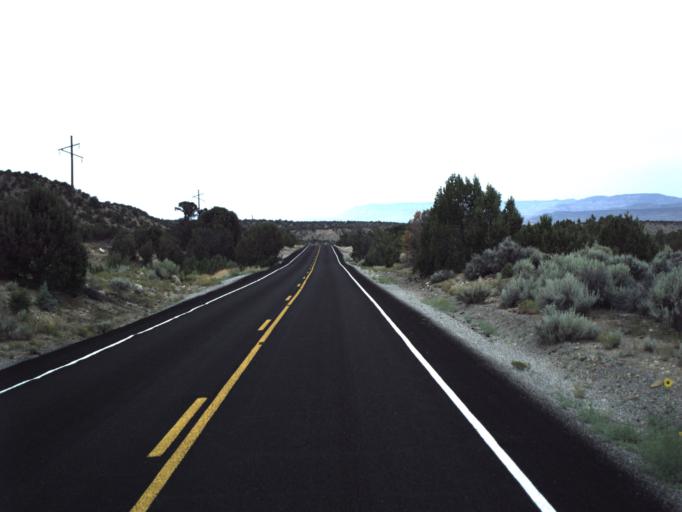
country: US
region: Utah
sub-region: Carbon County
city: East Carbon City
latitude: 39.4974
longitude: -110.4009
